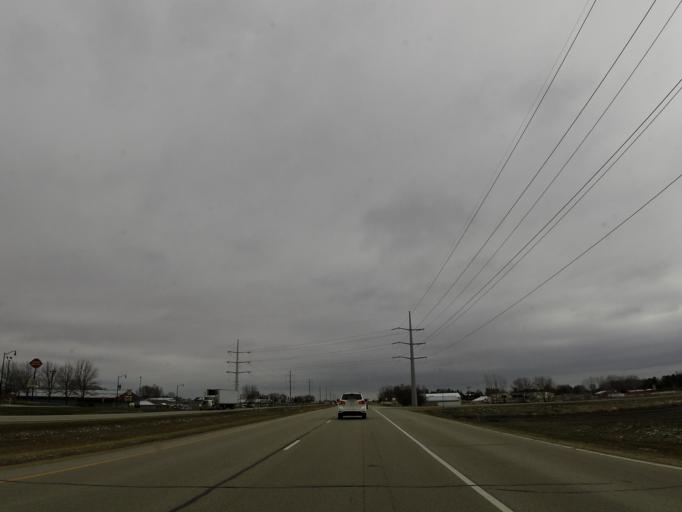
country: US
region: Minnesota
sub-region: Olmsted County
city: Byron
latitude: 44.0285
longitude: -92.6395
